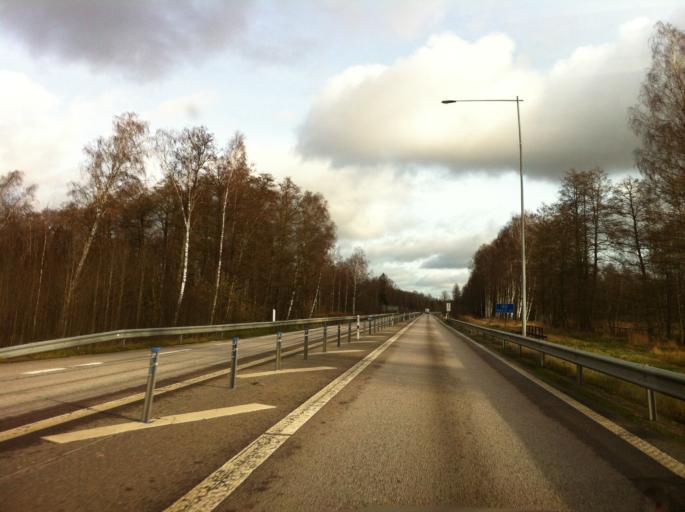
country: SE
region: Kronoberg
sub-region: Alvesta Kommun
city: Vislanda
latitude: 56.7237
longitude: 14.4653
